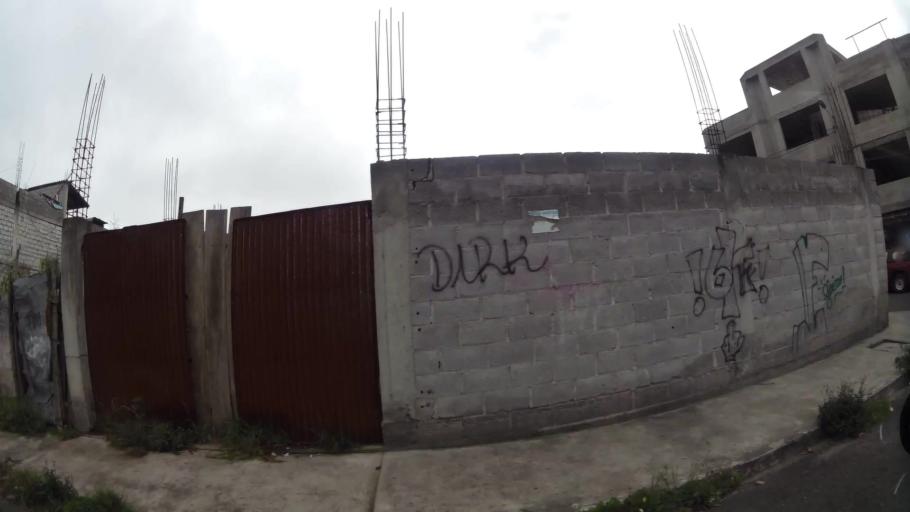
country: EC
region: Pichincha
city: Quito
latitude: -0.3130
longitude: -78.5537
